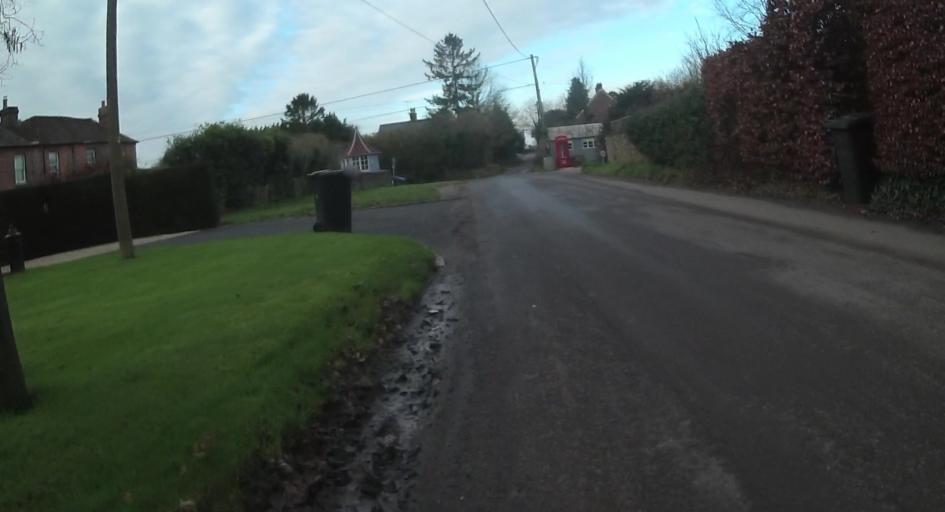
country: GB
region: England
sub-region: Hampshire
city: Basingstoke
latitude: 51.2758
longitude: -1.1524
